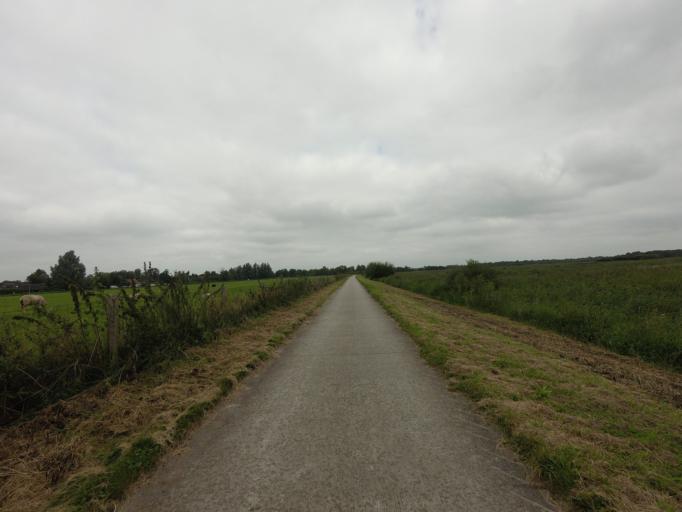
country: NL
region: Overijssel
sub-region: Gemeente Steenwijkerland
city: Oldemarkt
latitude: 52.7779
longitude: 5.9853
